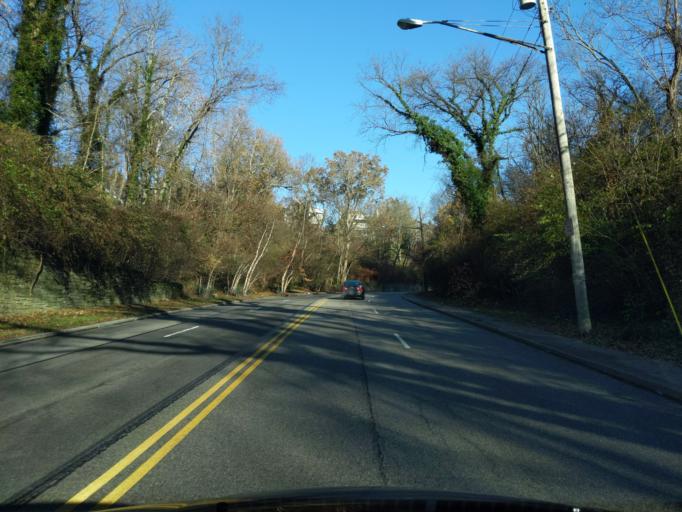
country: US
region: Kentucky
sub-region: Campbell County
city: Dayton
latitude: 39.1289
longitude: -84.4643
